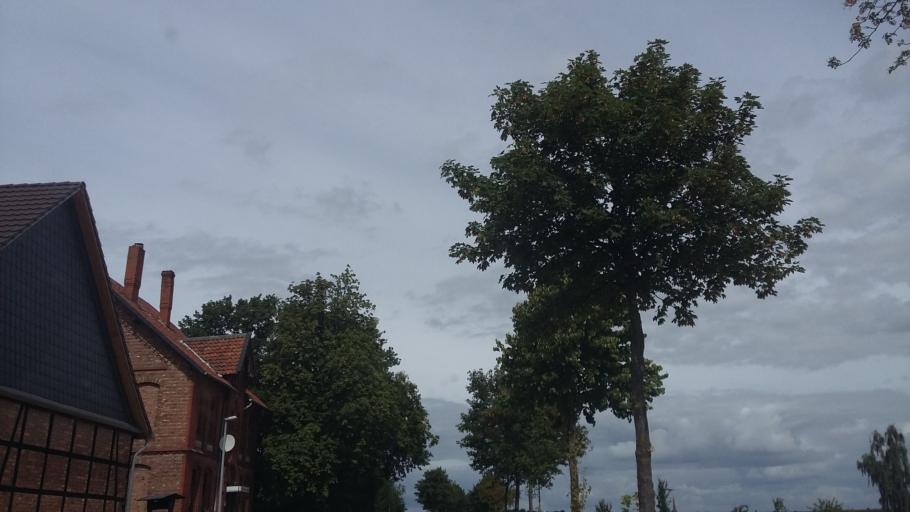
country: DE
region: Lower Saxony
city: Harsum
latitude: 52.1892
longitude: 10.0079
